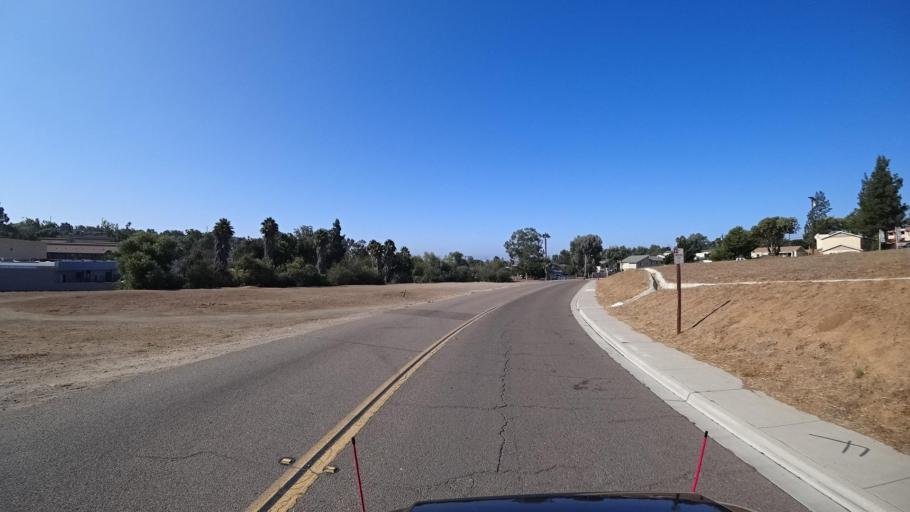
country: US
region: California
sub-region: San Diego County
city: Fallbrook
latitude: 33.3725
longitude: -117.2571
